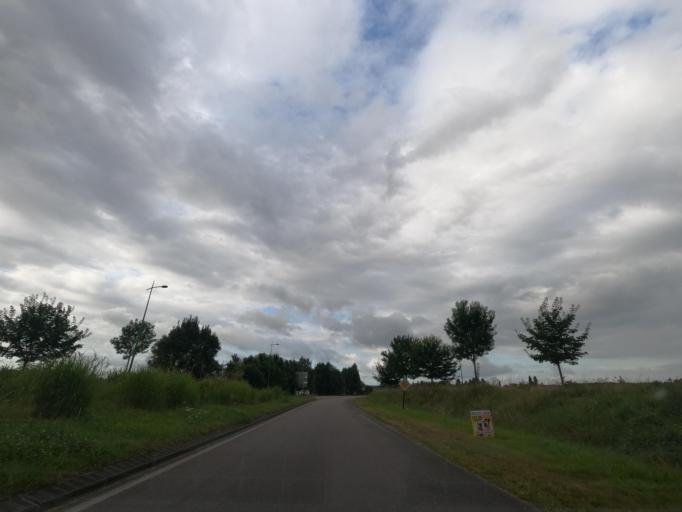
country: FR
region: Haute-Normandie
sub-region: Departement de l'Eure
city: Bourgtheroulde-Infreville
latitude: 49.3034
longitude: 0.8833
